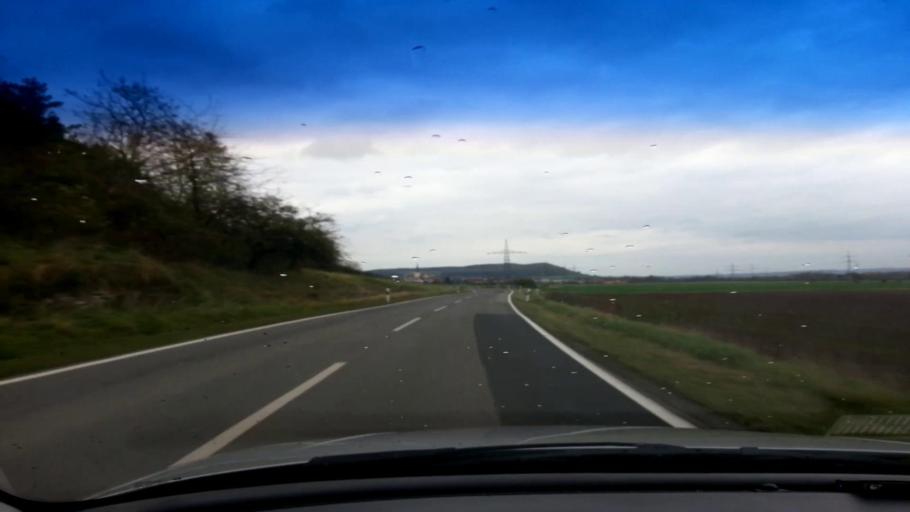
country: DE
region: Bavaria
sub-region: Regierungsbezirk Unterfranken
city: Stettfeld
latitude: 49.9768
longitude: 10.7050
